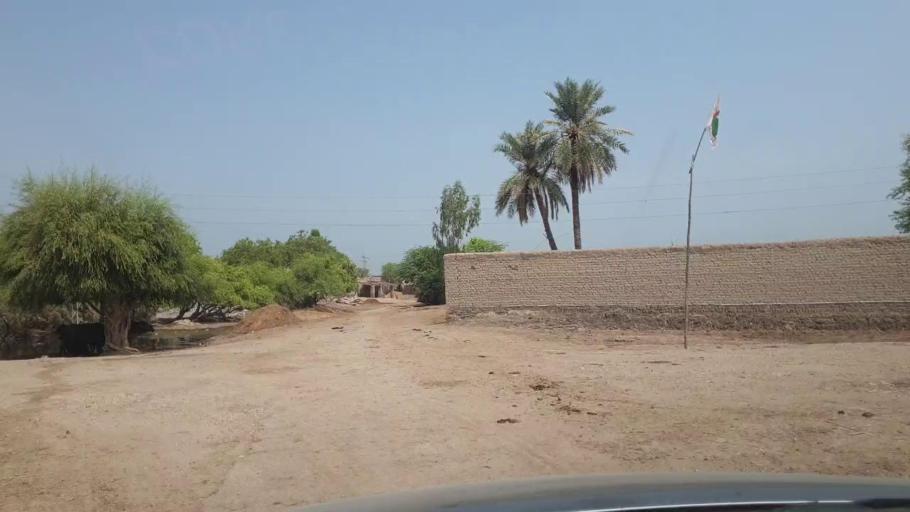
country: PK
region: Sindh
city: Garhi Yasin
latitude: 27.8371
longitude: 68.5392
